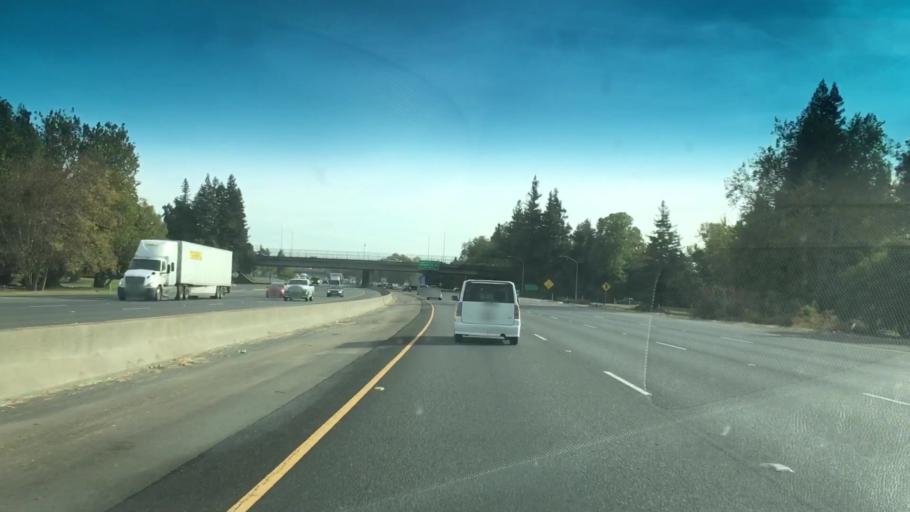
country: US
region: California
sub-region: Sacramento County
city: Parkway
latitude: 38.4979
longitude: -121.5173
